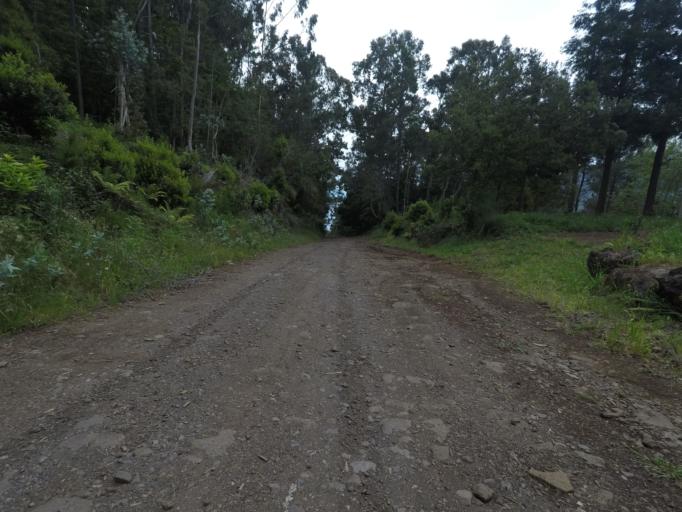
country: PT
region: Madeira
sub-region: Sao Vicente
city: Sao Vicente
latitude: 32.7771
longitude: -17.0480
